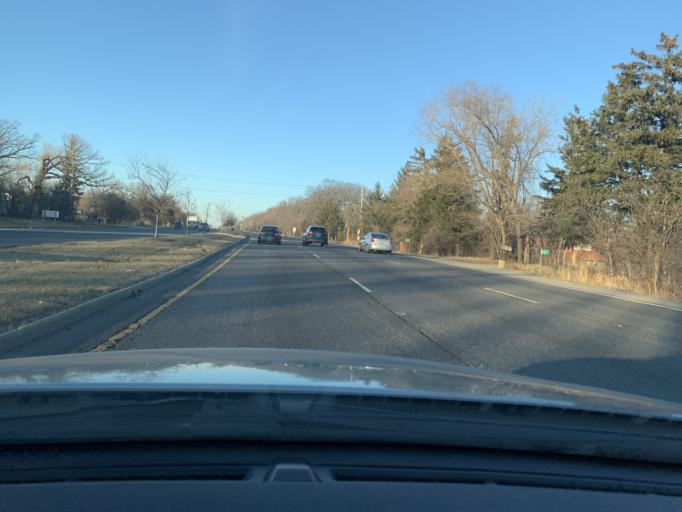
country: US
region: Illinois
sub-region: DuPage County
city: Bensenville
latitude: 41.9466
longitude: -87.9594
